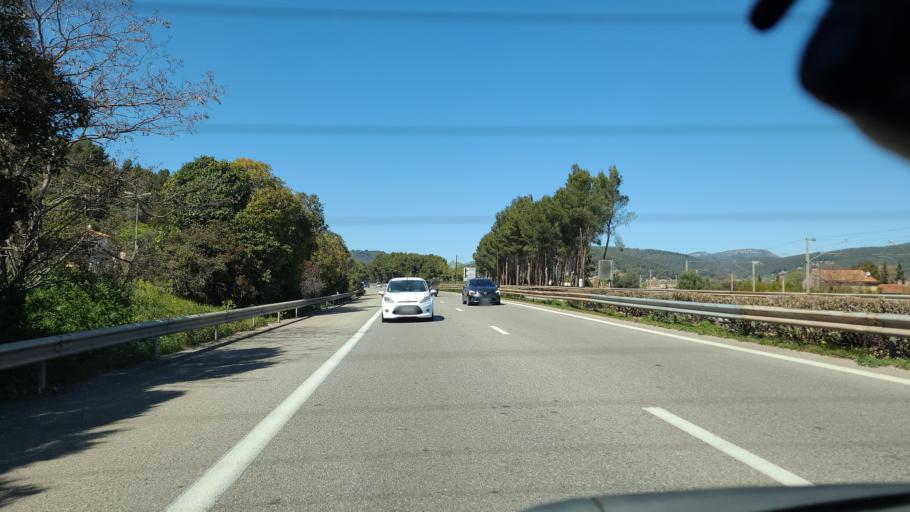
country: FR
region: Provence-Alpes-Cote d'Azur
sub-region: Departement du Var
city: Sollies-Ville
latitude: 43.1821
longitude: 6.0447
